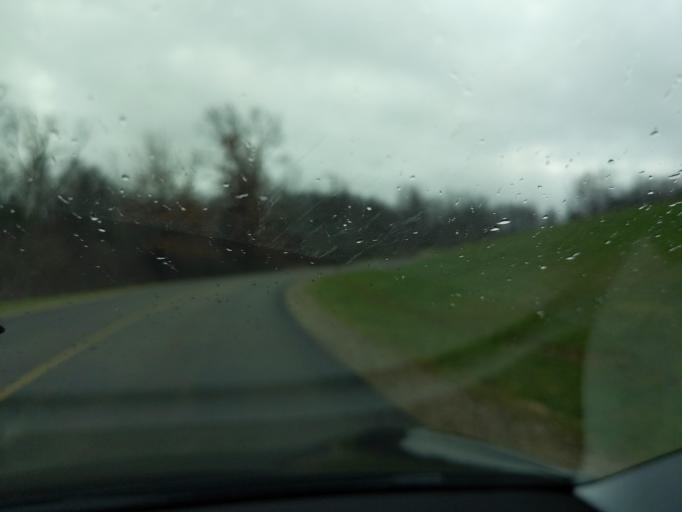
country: US
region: Michigan
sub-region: Jackson County
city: Spring Arbor
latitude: 42.2501
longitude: -84.5396
